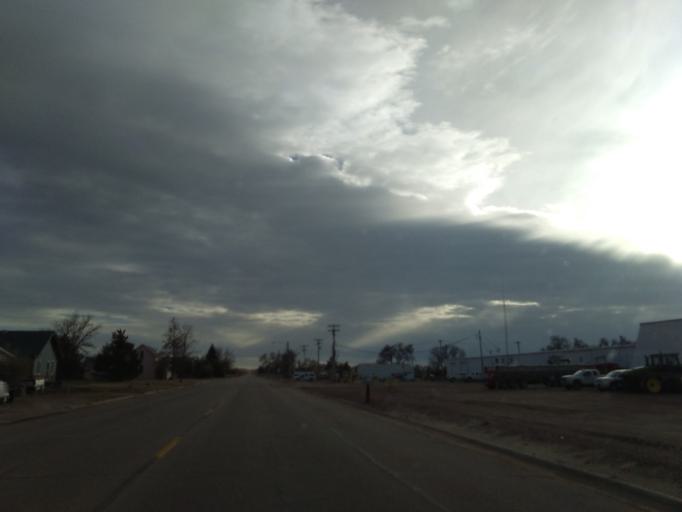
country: US
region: Nebraska
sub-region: Morrill County
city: Bridgeport
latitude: 41.6585
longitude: -103.0996
